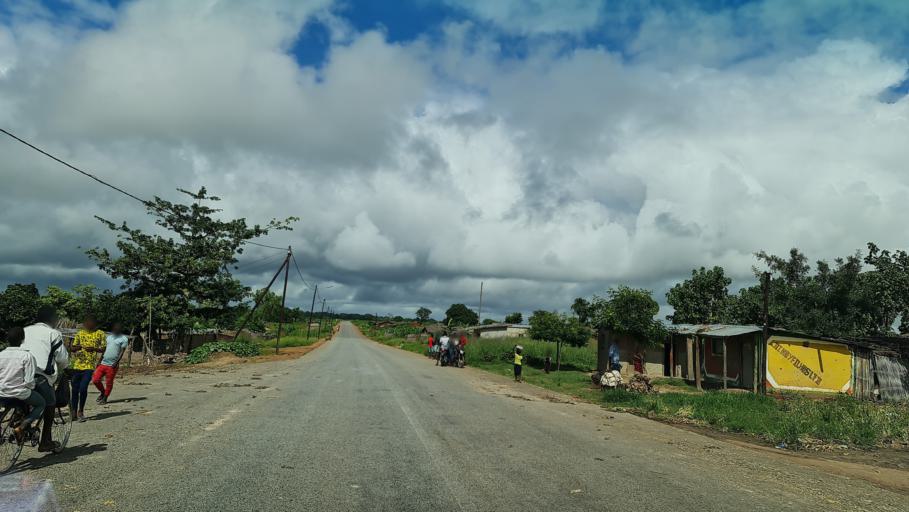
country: MZ
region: Nampula
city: Nampula
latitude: -15.0269
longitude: 38.4580
